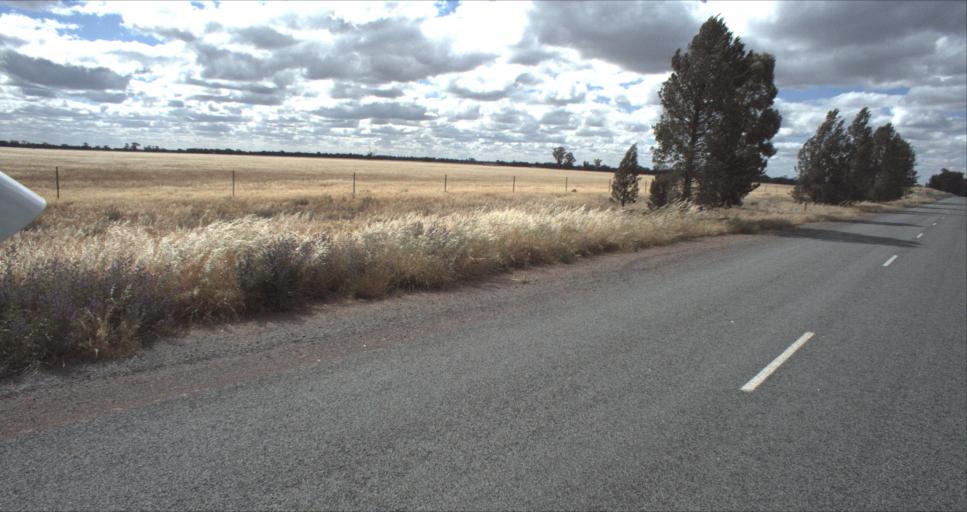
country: AU
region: New South Wales
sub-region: Leeton
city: Leeton
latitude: -34.6762
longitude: 146.3465
